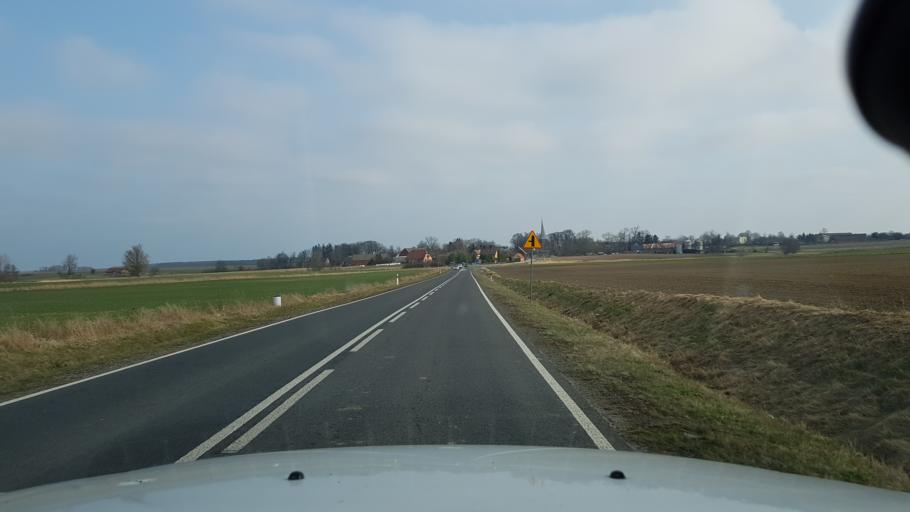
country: PL
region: West Pomeranian Voivodeship
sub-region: Powiat koszalinski
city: Sianow
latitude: 54.2890
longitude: 16.2716
